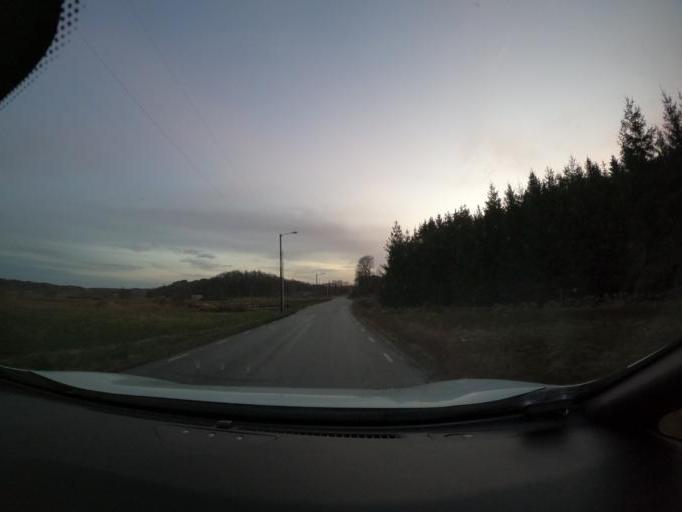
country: SE
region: Vaestra Goetaland
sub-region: Harryda Kommun
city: Molnlycke
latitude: 57.6051
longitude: 12.1377
